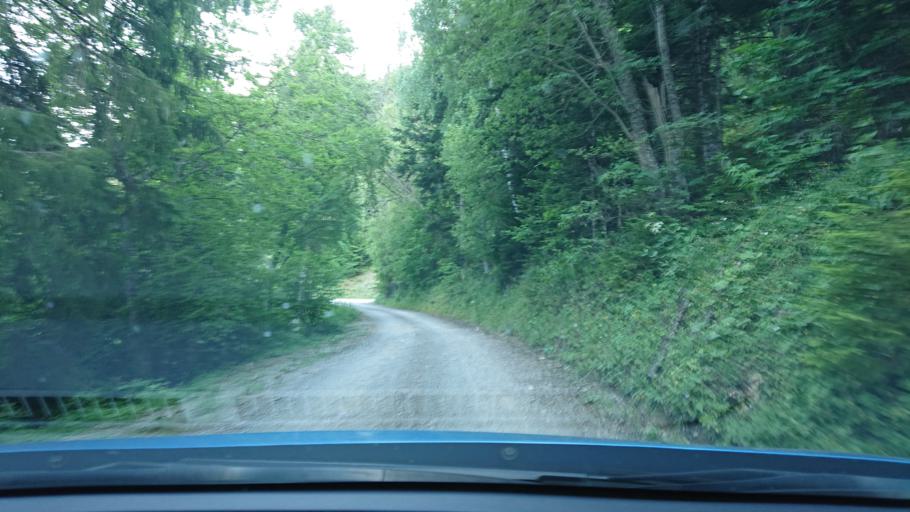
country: FR
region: Rhone-Alpes
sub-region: Departement de l'Isere
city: Mens
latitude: 44.7908
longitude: 5.8863
